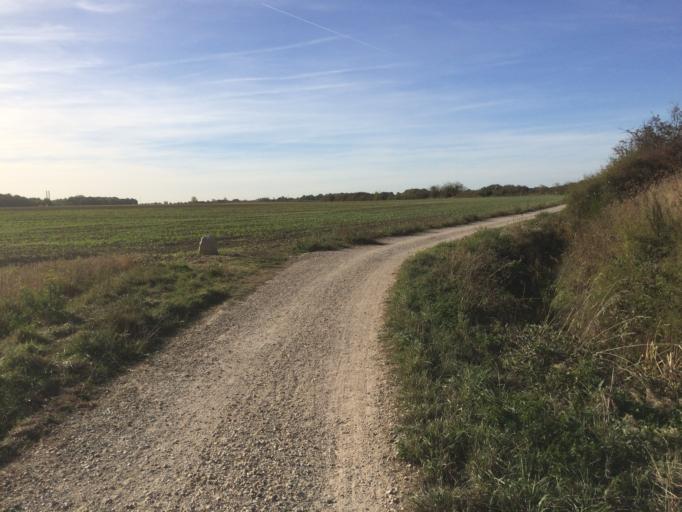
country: FR
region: Ile-de-France
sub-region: Departement de l'Essonne
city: Vauhallan
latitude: 48.7210
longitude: 2.2194
